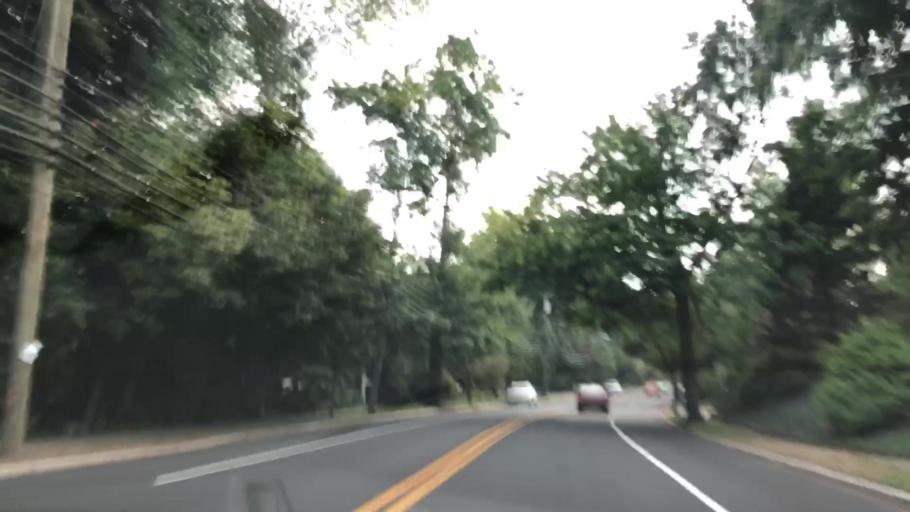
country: US
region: New Jersey
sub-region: Essex County
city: Upper Montclair
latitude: 40.8427
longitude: -74.1945
